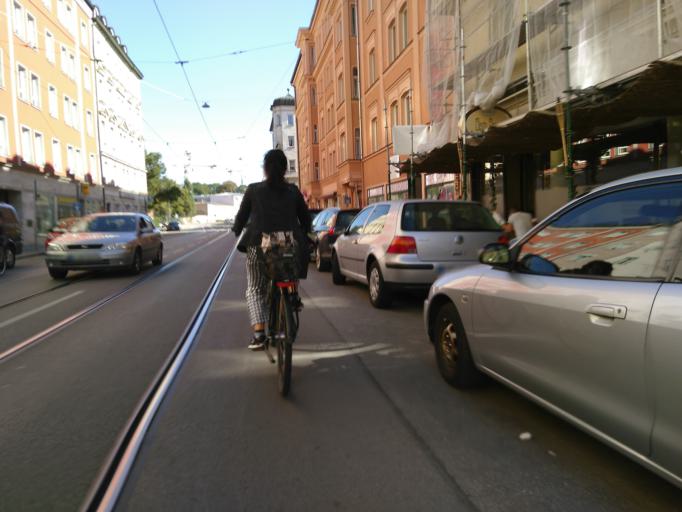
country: DE
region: Bavaria
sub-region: Upper Bavaria
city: Munich
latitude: 48.1256
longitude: 11.5792
